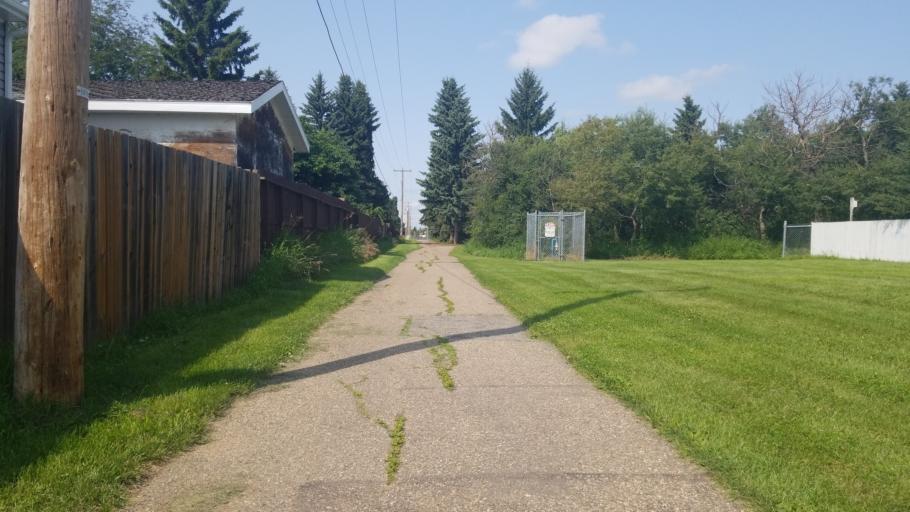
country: CA
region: Saskatchewan
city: Lloydminster
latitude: 53.2714
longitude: -110.0176
